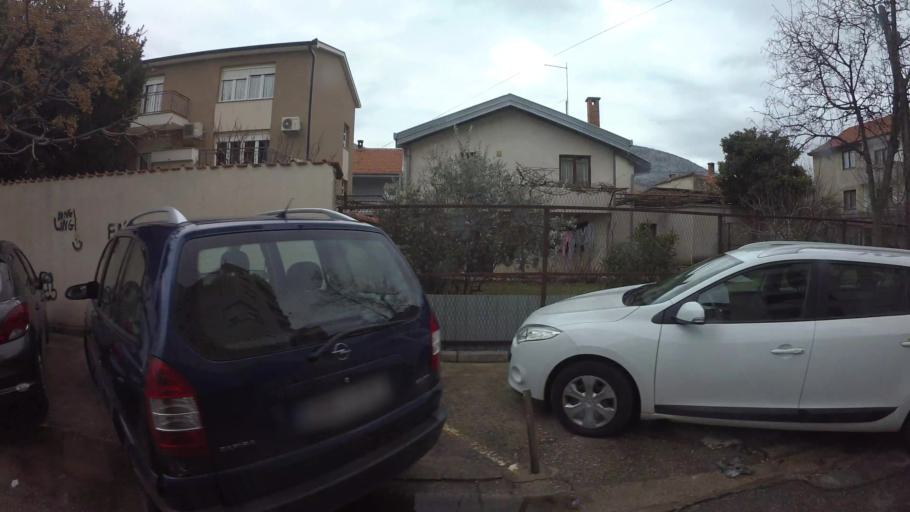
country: BA
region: Federation of Bosnia and Herzegovina
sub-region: Hercegovacko-Bosanski Kanton
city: Mostar
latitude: 43.3416
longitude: 17.8094
